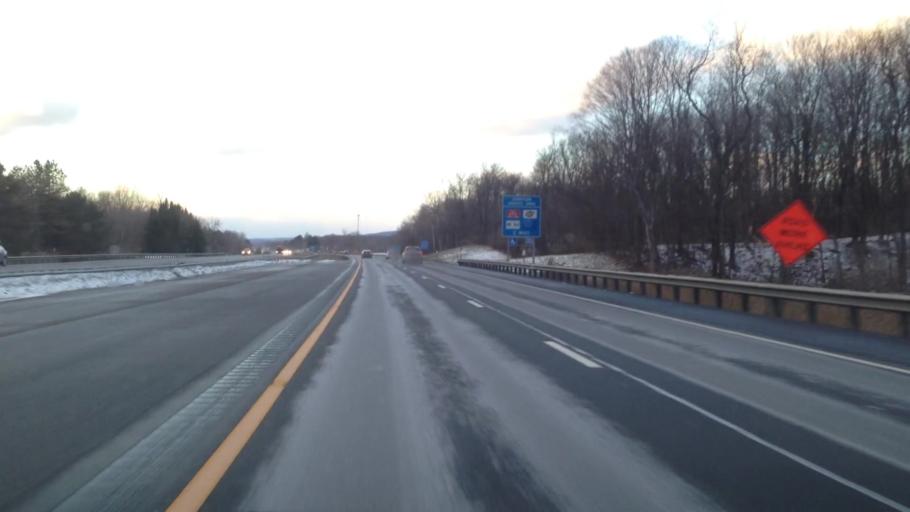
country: US
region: New York
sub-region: Herkimer County
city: Frankfort
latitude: 43.0559
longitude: -75.0679
